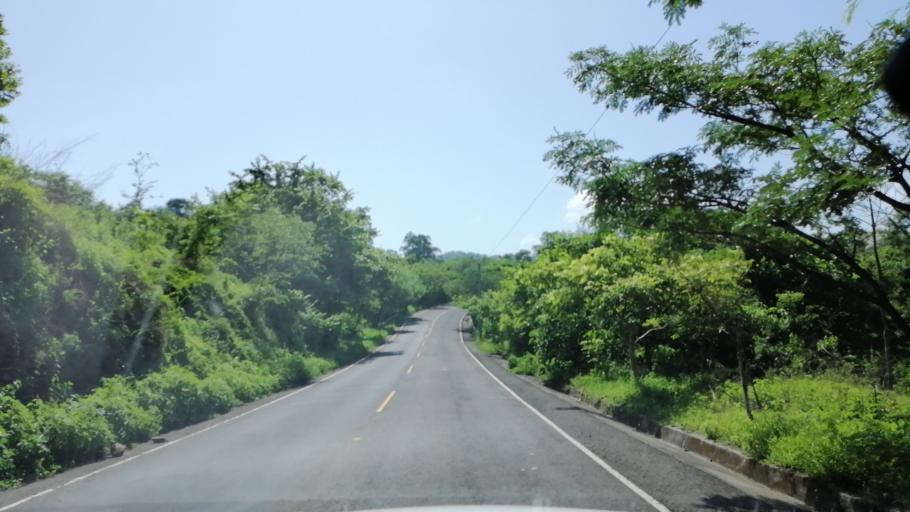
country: HN
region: Lempira
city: La Virtud
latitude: 13.9581
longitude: -88.7578
